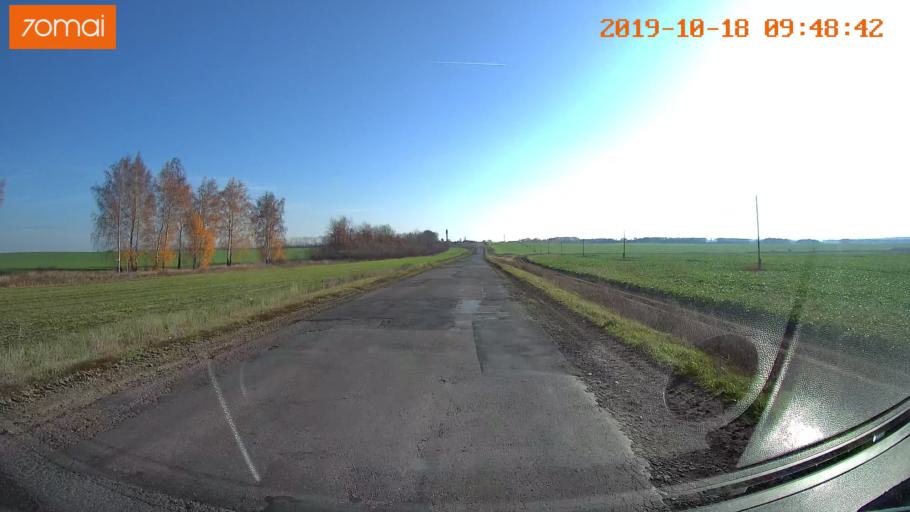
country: RU
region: Tula
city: Kazachka
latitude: 53.3170
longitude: 38.2553
